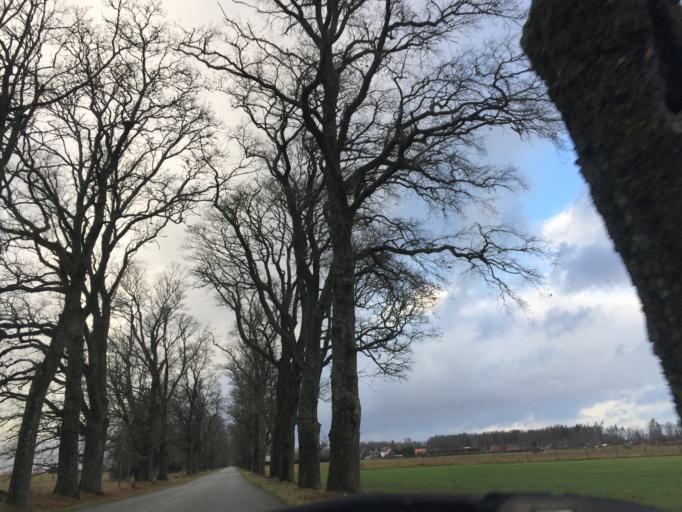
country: LV
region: Burtnieki
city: Matisi
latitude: 57.6878
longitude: 25.2859
